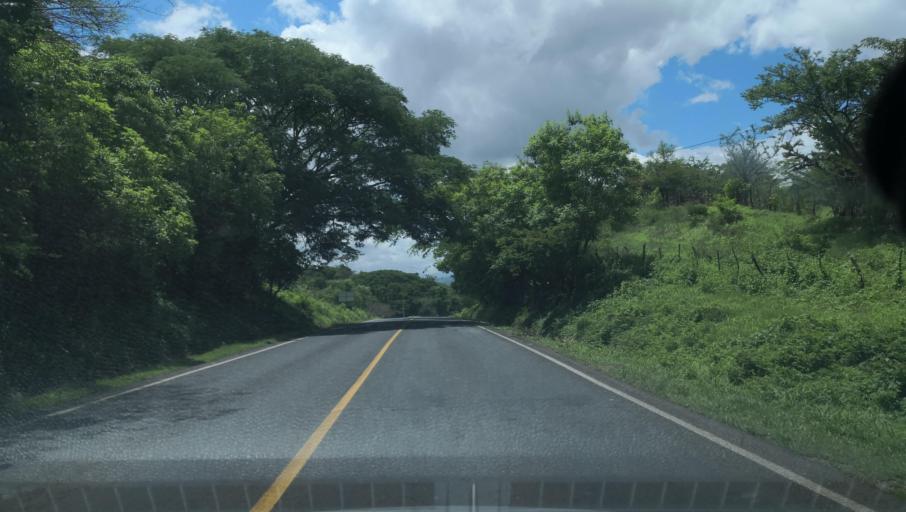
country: NI
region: Esteli
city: Condega
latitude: 13.3913
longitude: -86.4013
